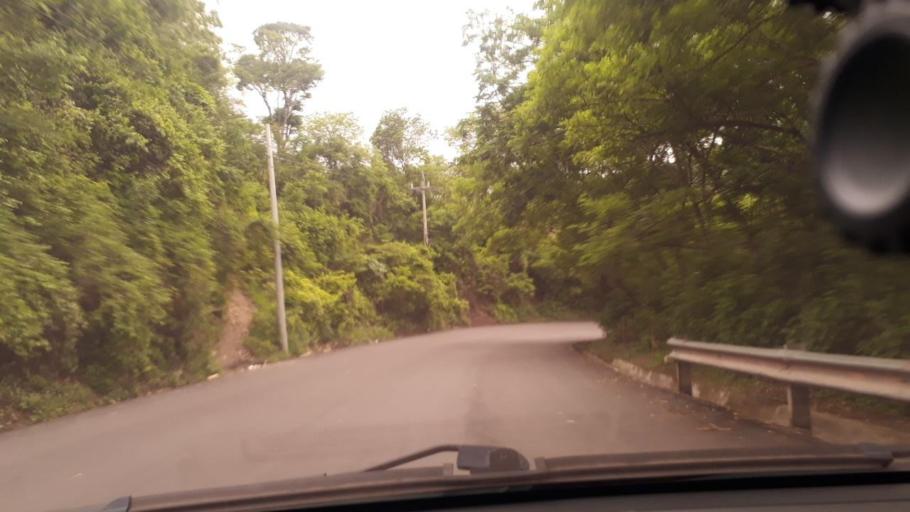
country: GT
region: Chiquimula
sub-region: Municipio de San Juan Ermita
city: San Juan Ermita
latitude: 14.7462
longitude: -89.4623
